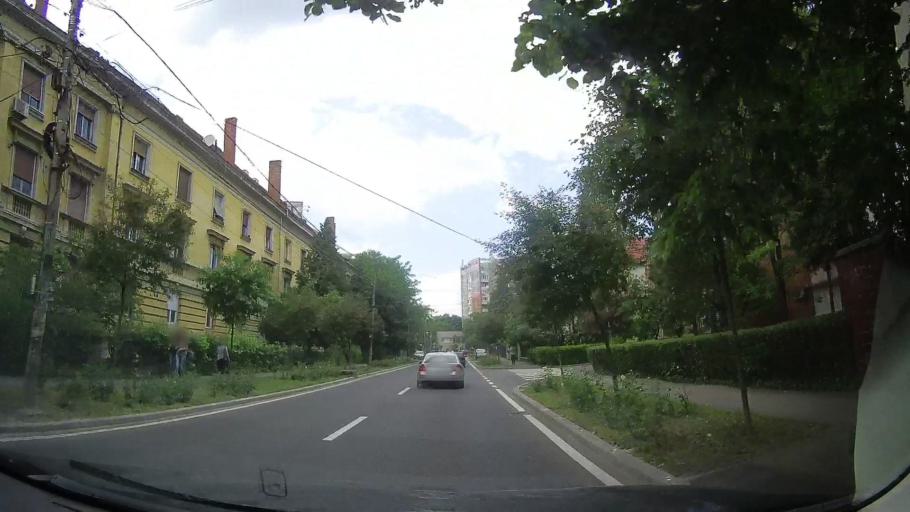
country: RO
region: Timis
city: Timisoara
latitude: 45.7579
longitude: 21.2379
